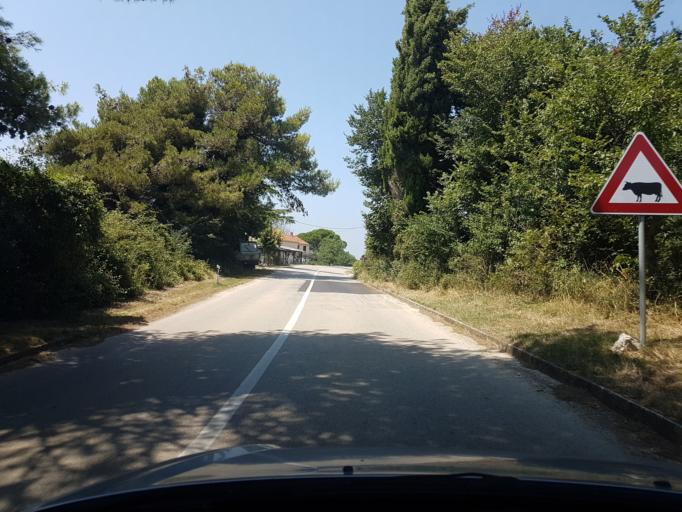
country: HR
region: Istarska
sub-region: Grad Rovinj
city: Rovinj
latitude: 45.1435
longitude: 13.7034
